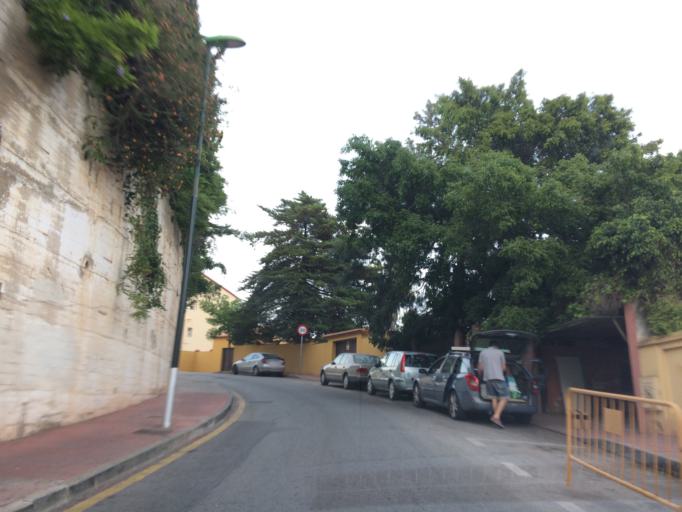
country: ES
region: Andalusia
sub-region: Provincia de Malaga
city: Malaga
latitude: 36.7279
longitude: -4.3837
